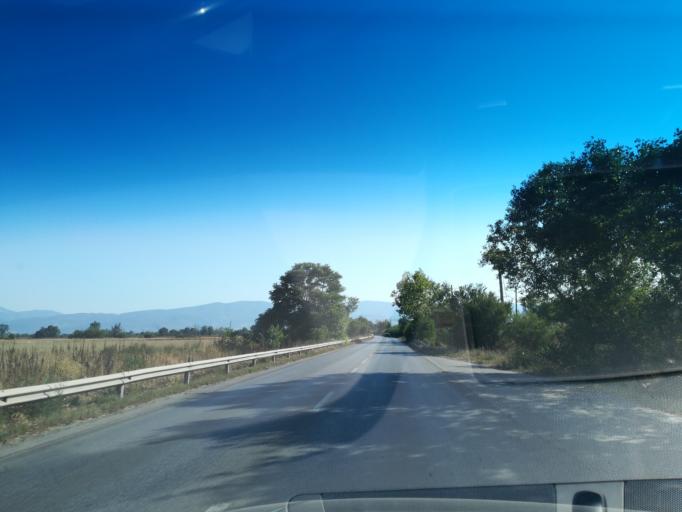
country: BG
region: Plovdiv
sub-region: Obshtina Plovdiv
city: Plovdiv
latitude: 42.1598
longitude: 24.8116
